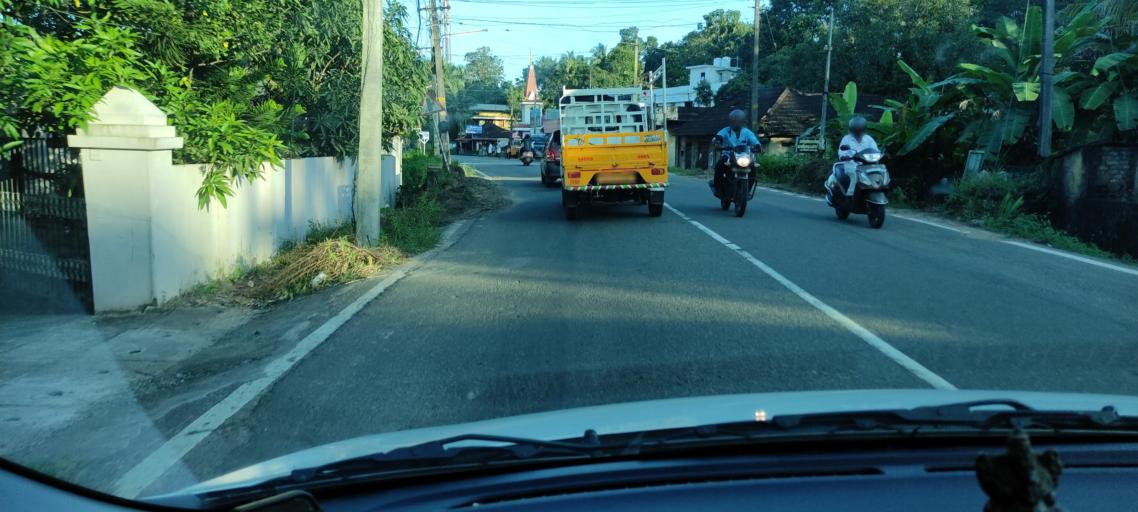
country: IN
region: Kerala
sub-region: Pattanamtitta
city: Adur
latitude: 9.1429
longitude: 76.7761
